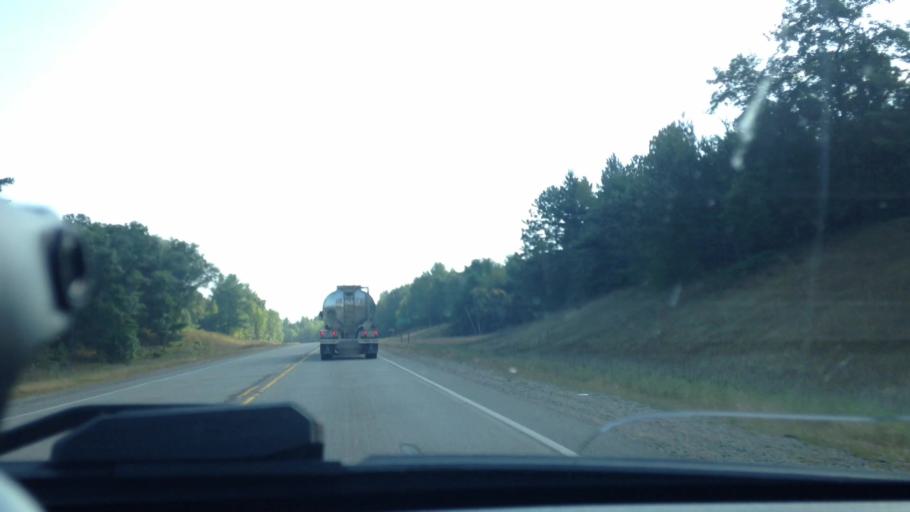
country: US
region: Wisconsin
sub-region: Marinette County
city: Niagara
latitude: 45.6420
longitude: -87.9743
